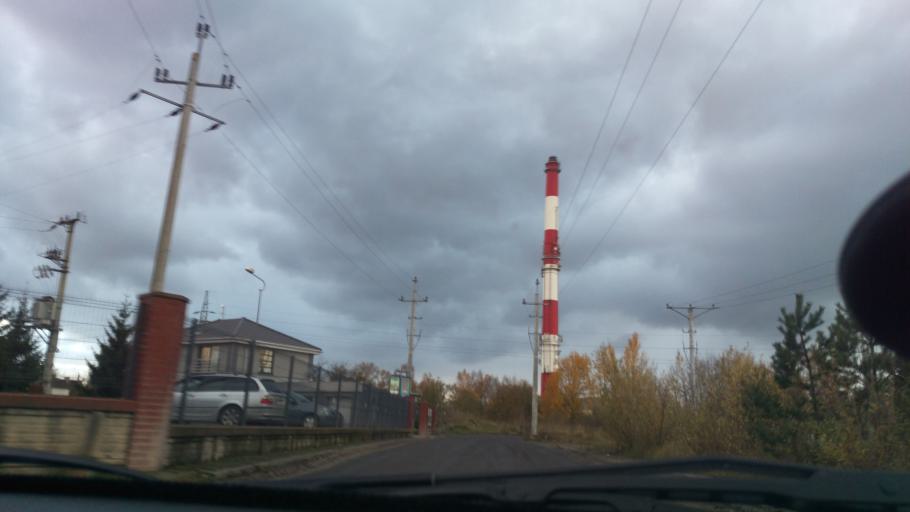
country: PL
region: West Pomeranian Voivodeship
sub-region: Szczecin
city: Szczecin
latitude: 53.3708
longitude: 14.6772
